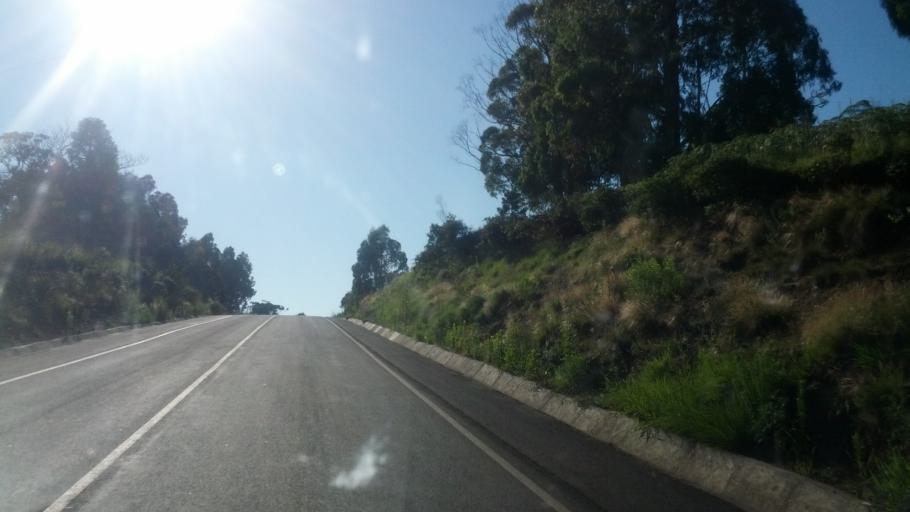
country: BR
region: Santa Catarina
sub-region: Lages
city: Lages
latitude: -27.9287
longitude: -50.5350
